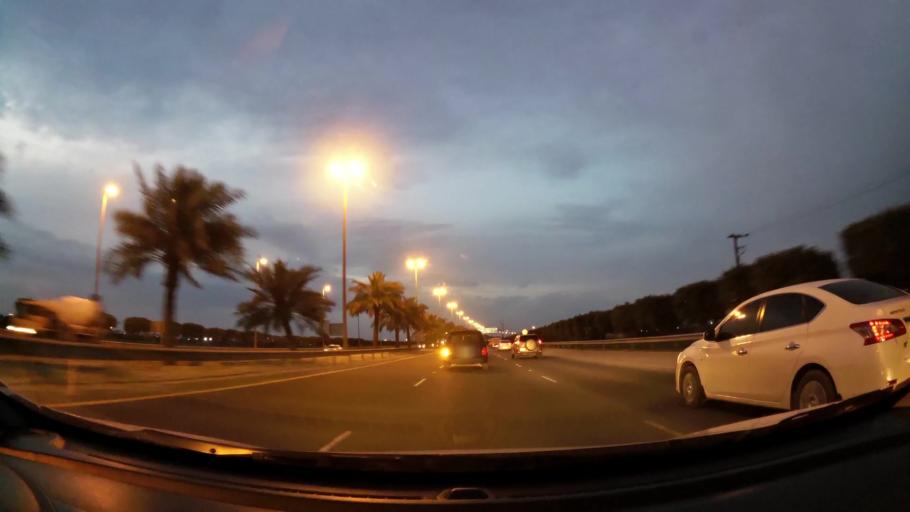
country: BH
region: Northern
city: Madinat `Isa
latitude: 26.1732
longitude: 50.5025
